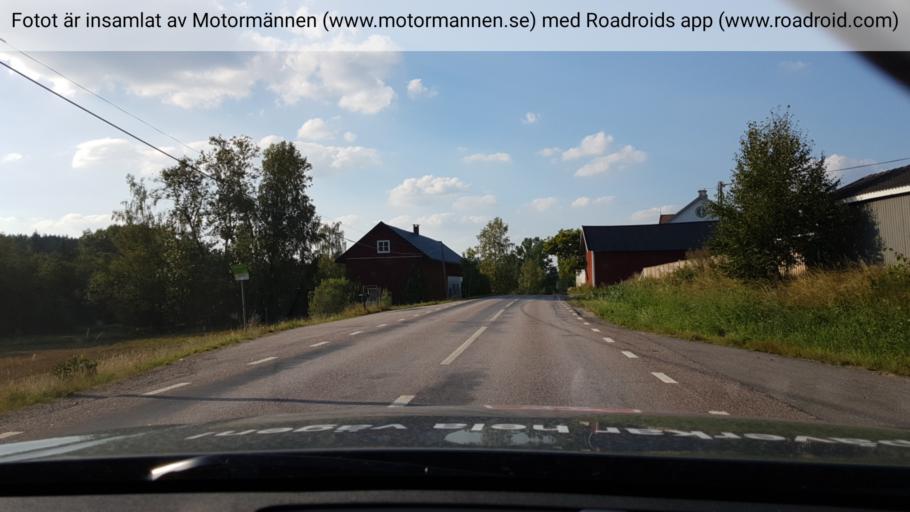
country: SE
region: Soedermanland
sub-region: Strangnas Kommun
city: Mariefred
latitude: 59.2182
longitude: 17.1704
